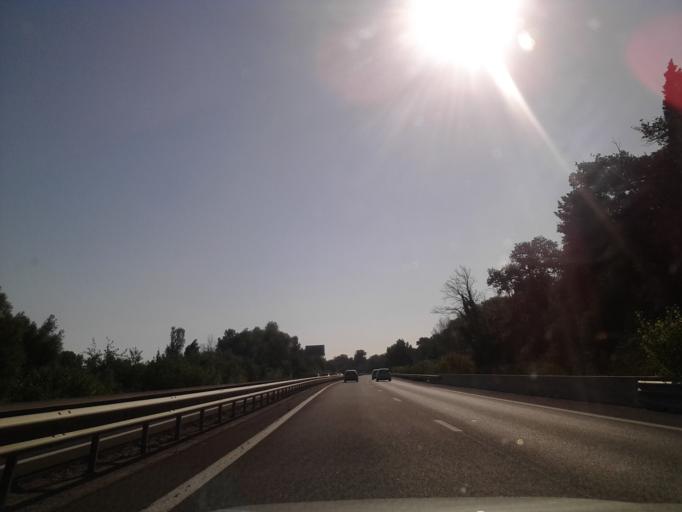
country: FR
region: Languedoc-Roussillon
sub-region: Departement des Pyrenees-Orientales
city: Baho
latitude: 42.6896
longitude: 2.8249
